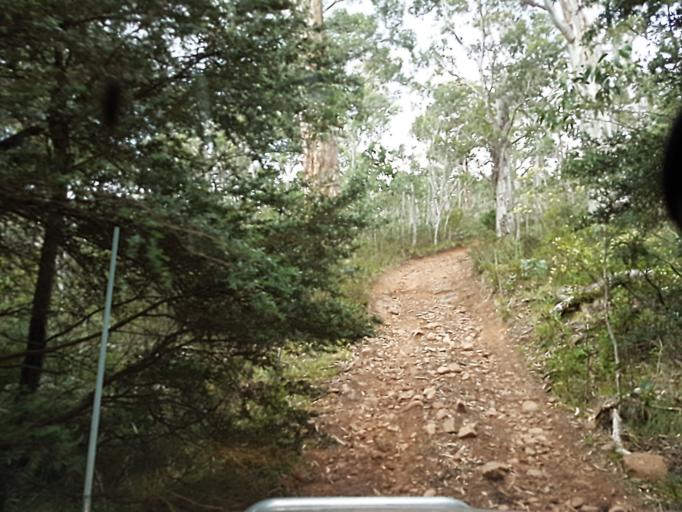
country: AU
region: New South Wales
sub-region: Snowy River
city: Jindabyne
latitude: -36.8744
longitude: 148.1727
